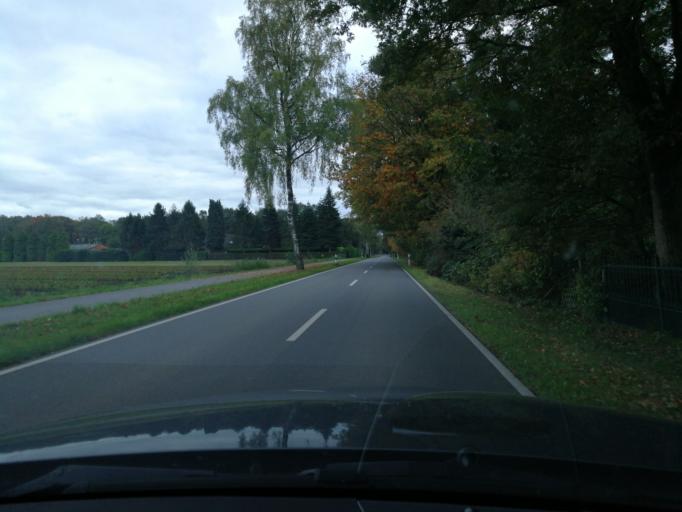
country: NL
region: Limburg
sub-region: Gemeente Venlo
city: Arcen
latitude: 51.4811
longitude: 6.2208
